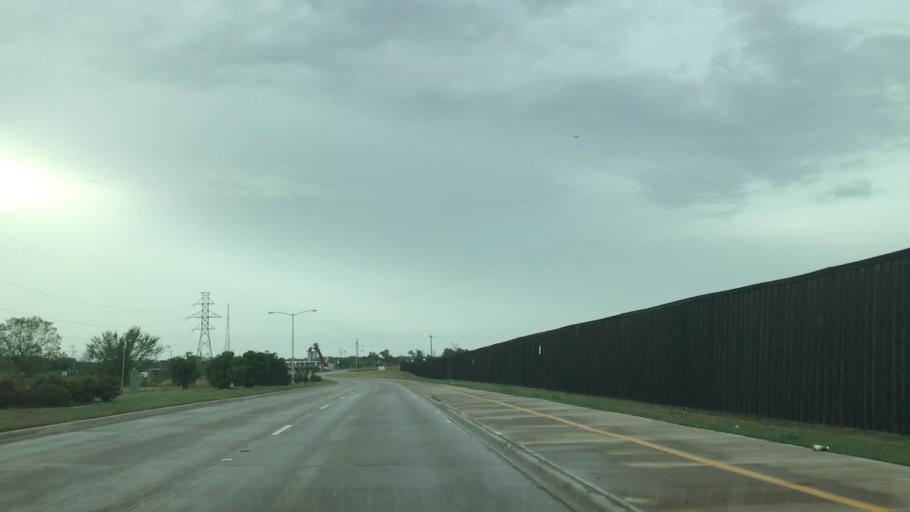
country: US
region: Texas
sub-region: Denton County
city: Lewisville
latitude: 33.0471
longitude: -96.9784
